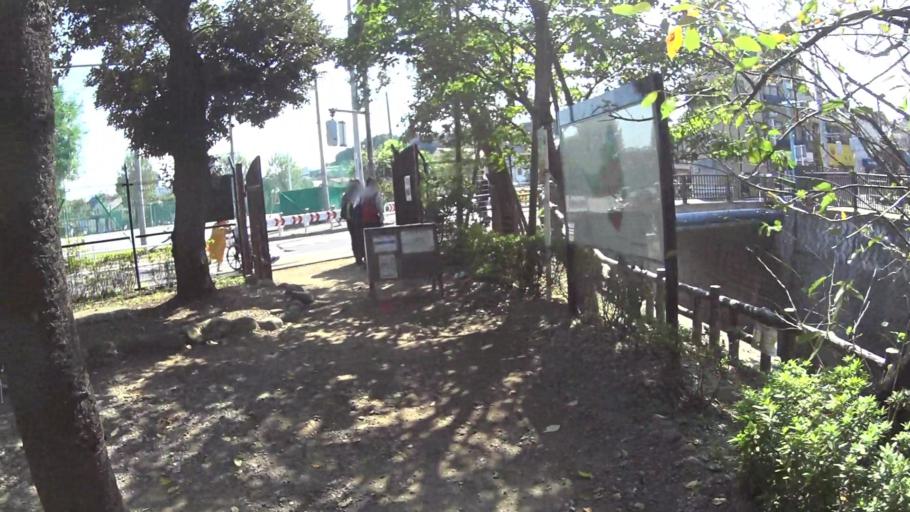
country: JP
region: Tokyo
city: Tokyo
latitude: 35.7207
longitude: 139.6755
